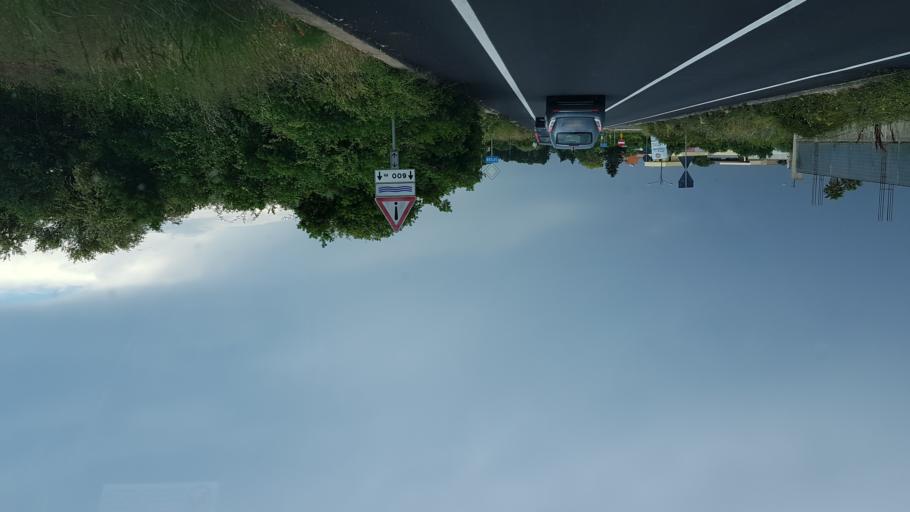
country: IT
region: Apulia
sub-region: Provincia di Lecce
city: Porto Cesareo
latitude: 40.2947
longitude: 17.8565
